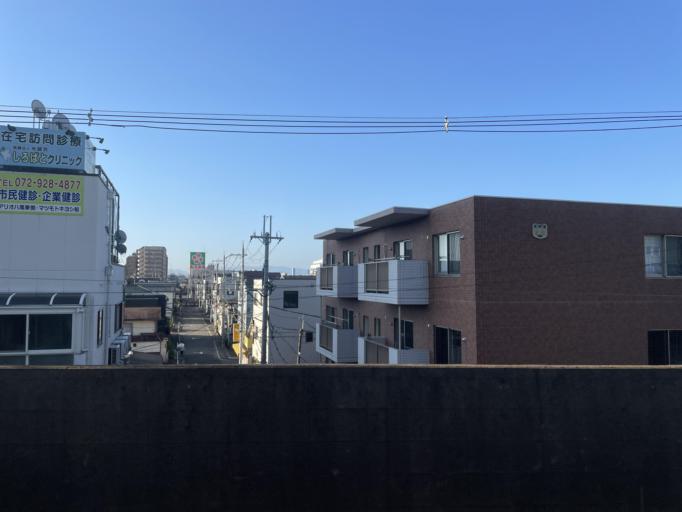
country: JP
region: Osaka
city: Yao
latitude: 34.6286
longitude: 135.6071
